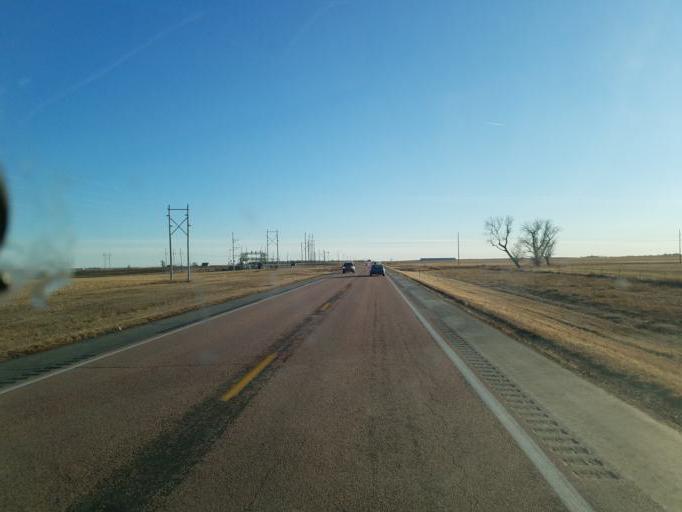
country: US
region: South Dakota
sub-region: Bon Homme County
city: Tyndall
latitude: 43.1430
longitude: -97.9705
